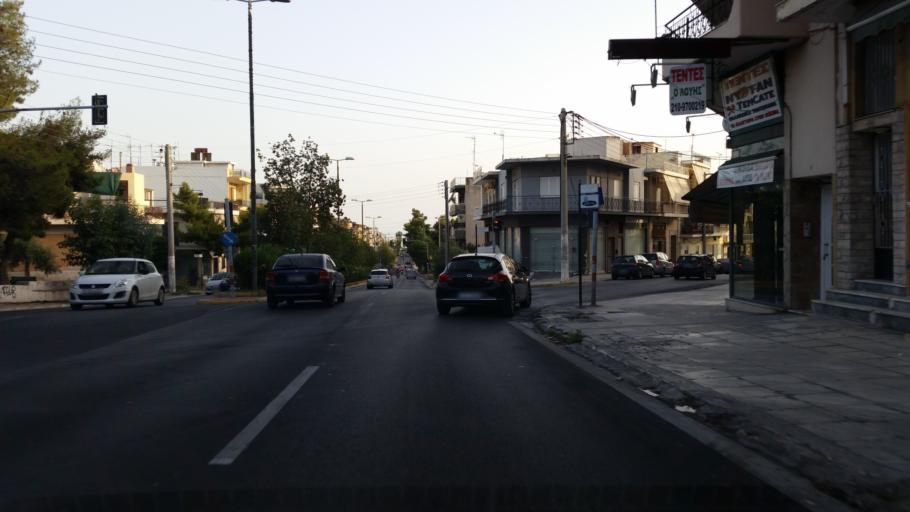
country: GR
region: Attica
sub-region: Nomarchia Athinas
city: Ilioupoli
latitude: 37.9418
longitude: 23.7620
